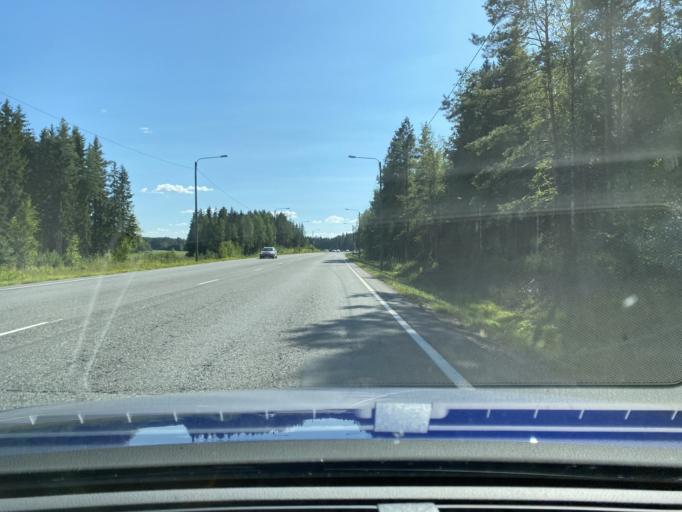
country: FI
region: Varsinais-Suomi
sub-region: Turku
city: Lieto
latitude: 60.5934
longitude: 22.4683
